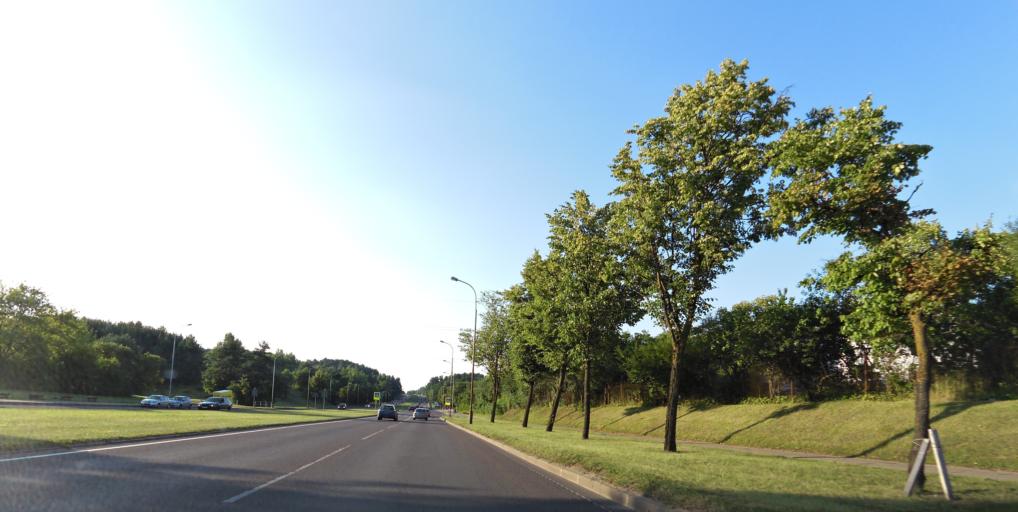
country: LT
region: Vilnius County
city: Seskine
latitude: 54.7204
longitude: 25.2708
